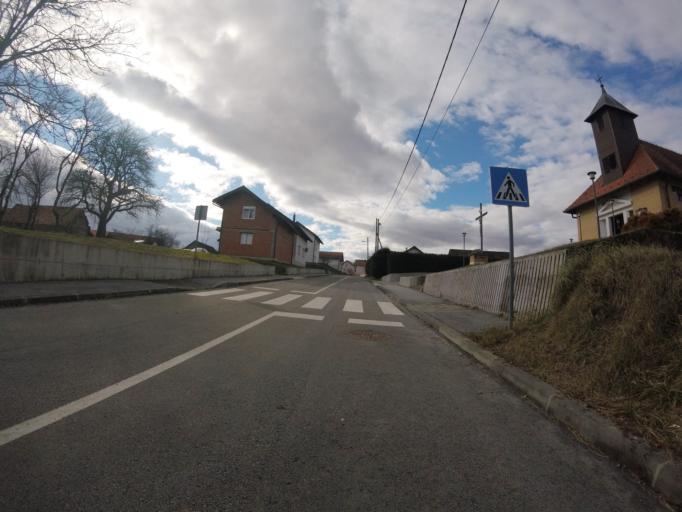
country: HR
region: Zagrebacka
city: Mraclin
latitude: 45.6358
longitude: 16.0581
